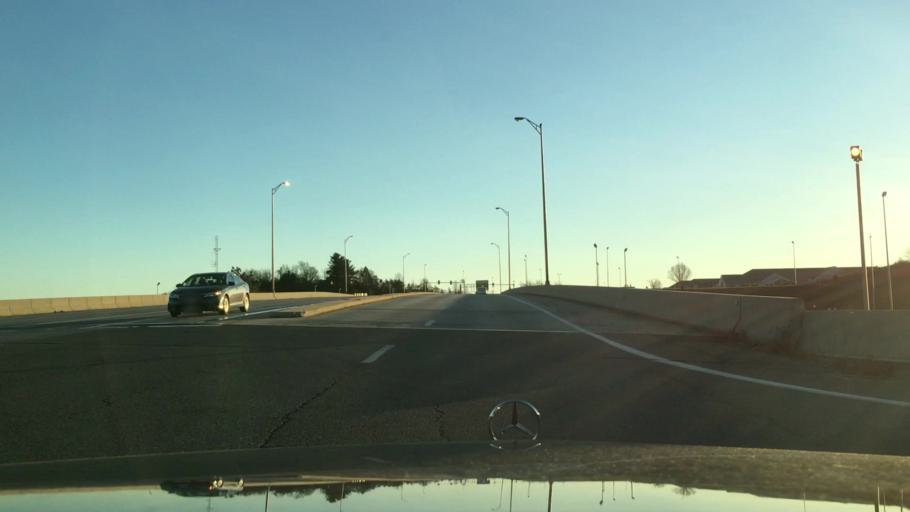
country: US
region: Virginia
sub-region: Montgomery County
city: Merrimac
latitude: 37.1940
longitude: -80.4030
